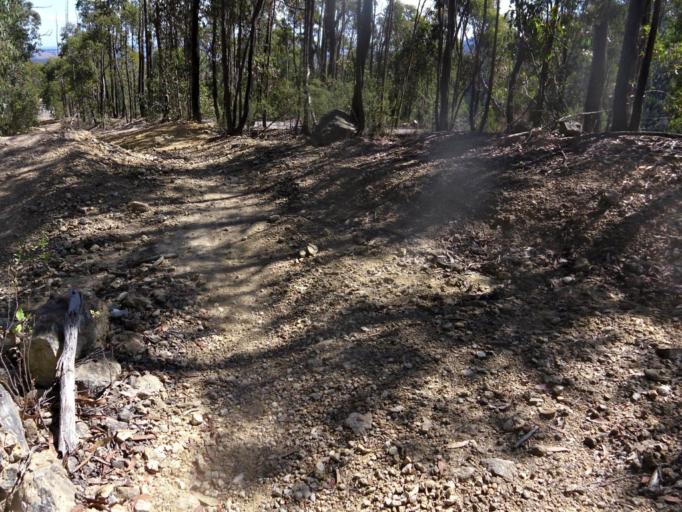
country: AU
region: Victoria
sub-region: Nillumbik
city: Saint Andrews
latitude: -37.5259
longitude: 145.3005
